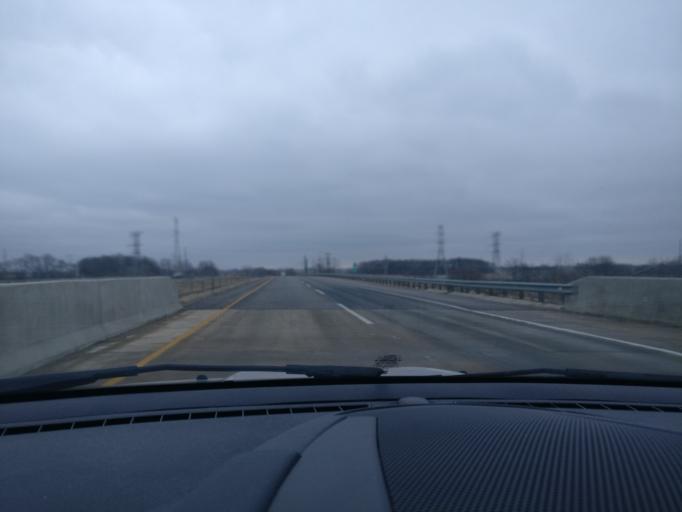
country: US
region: Illinois
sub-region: Whiteside County
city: Rock Falls
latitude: 41.7663
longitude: -89.6122
